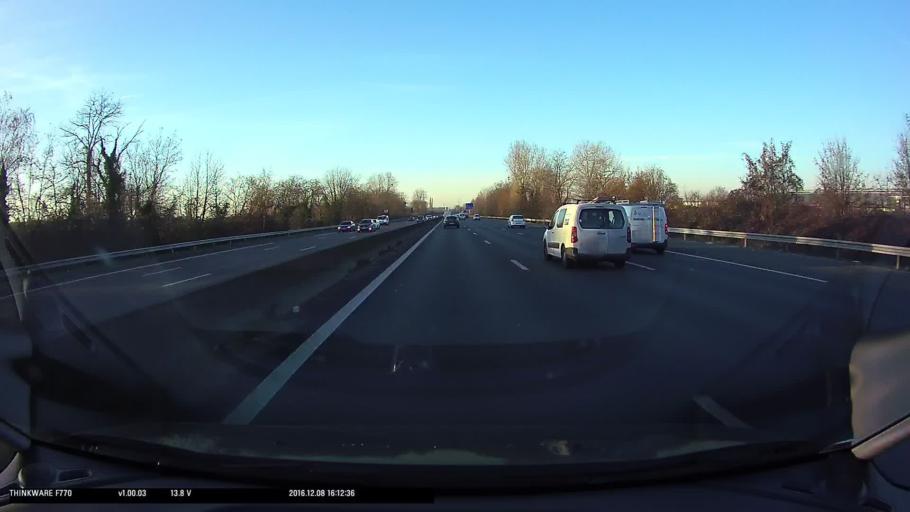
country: FR
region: Ile-de-France
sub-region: Departement du Val-d'Oise
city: Pierrelaye
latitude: 49.0194
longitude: 2.1395
